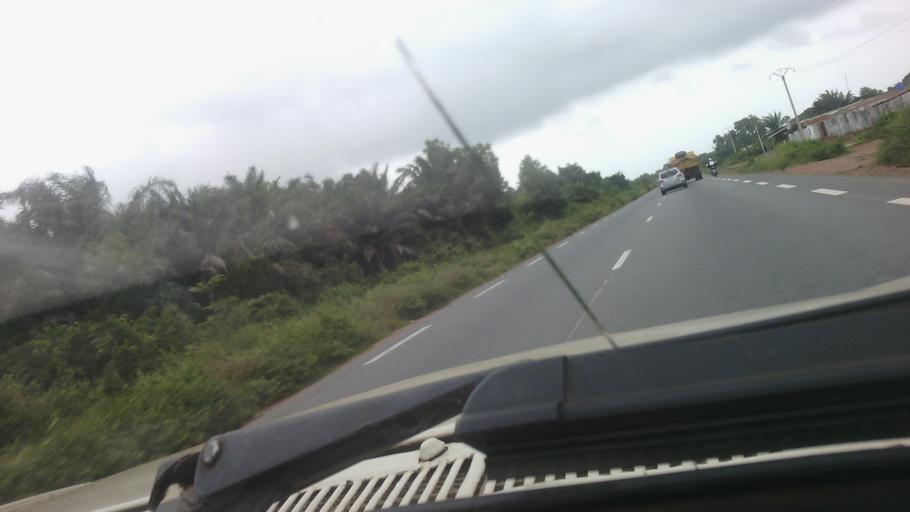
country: BJ
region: Atlantique
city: Ouidah
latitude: 6.3721
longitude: 2.0333
